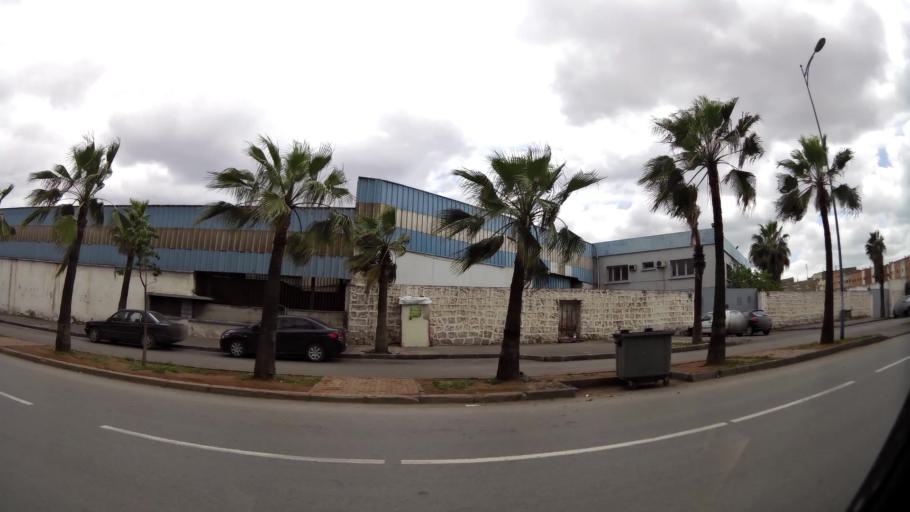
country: MA
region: Grand Casablanca
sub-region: Casablanca
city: Casablanca
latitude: 33.5879
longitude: -7.5457
